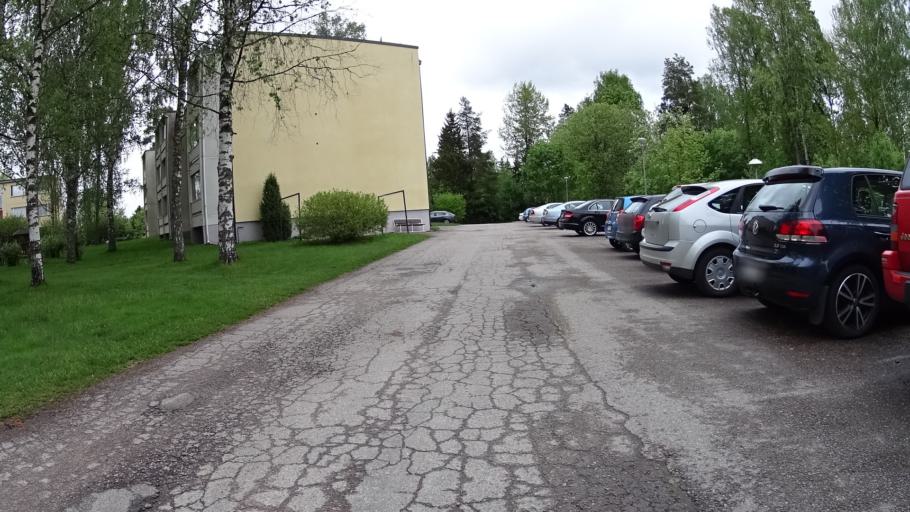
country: FI
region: Uusimaa
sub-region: Helsinki
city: Kauniainen
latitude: 60.2319
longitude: 24.7401
